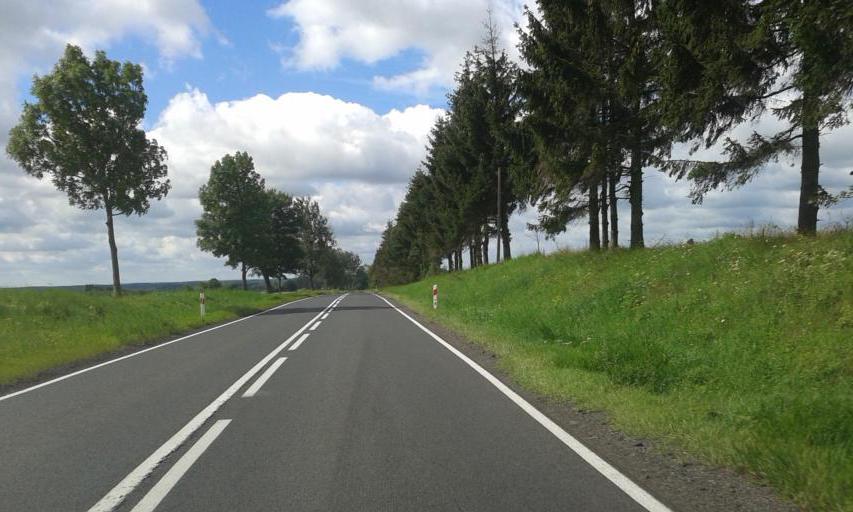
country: PL
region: West Pomeranian Voivodeship
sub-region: Powiat drawski
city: Czaplinek
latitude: 53.5768
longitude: 16.2718
